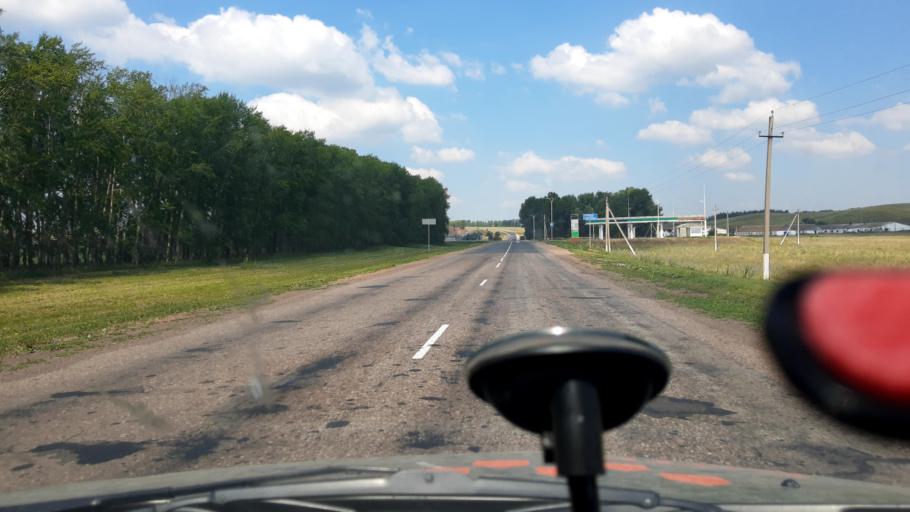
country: RU
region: Bashkortostan
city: Chekmagush
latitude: 54.8956
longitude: 54.5818
